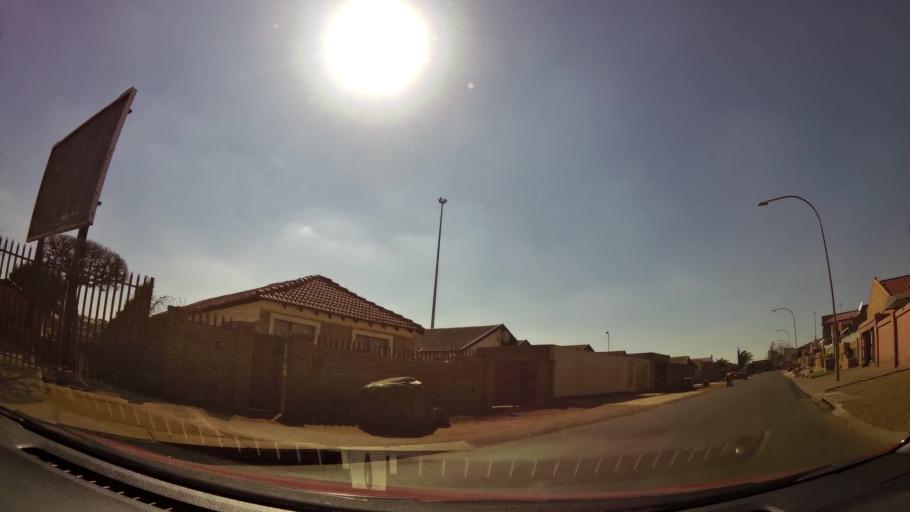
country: ZA
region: Gauteng
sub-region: City of Johannesburg Metropolitan Municipality
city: Soweto
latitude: -26.2339
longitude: 27.8228
